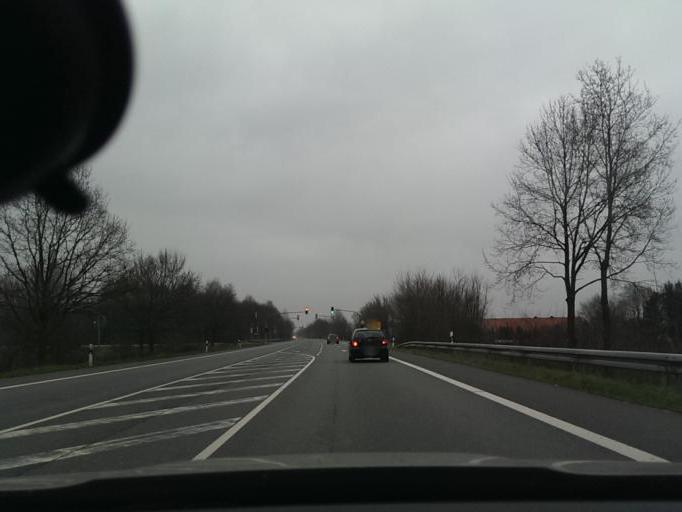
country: DE
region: North Rhine-Westphalia
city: Rietberg
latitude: 51.7904
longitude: 8.4284
